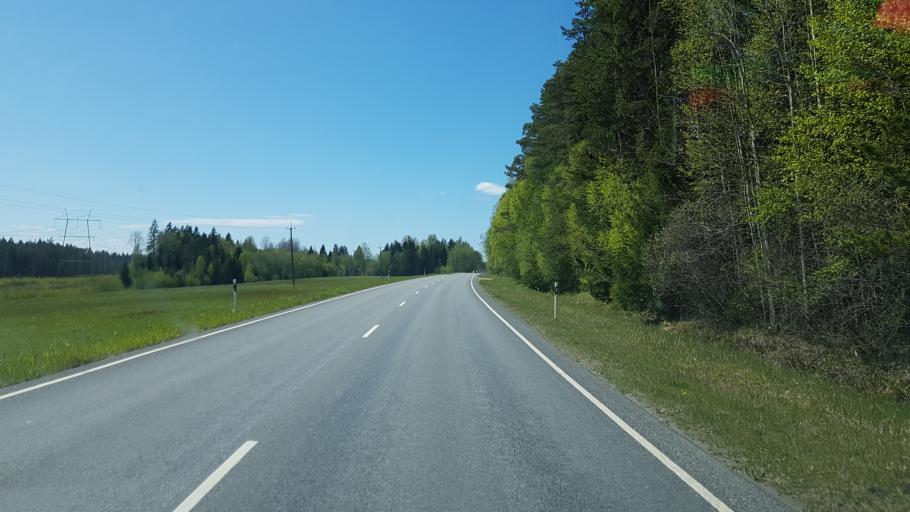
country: EE
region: Viljandimaa
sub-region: Abja vald
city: Abja-Paluoja
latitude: 58.2669
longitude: 25.2582
